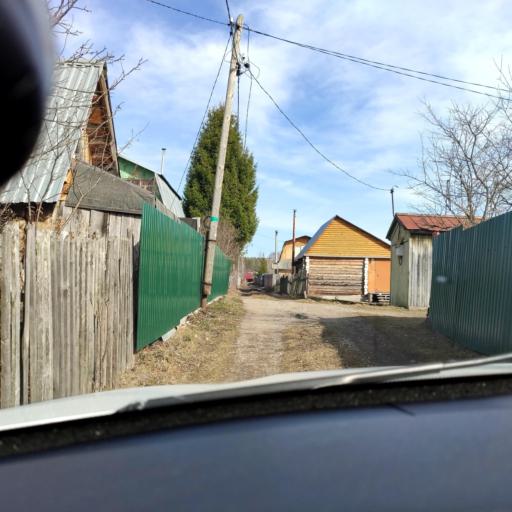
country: RU
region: Perm
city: Overyata
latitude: 58.0577
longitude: 55.9809
